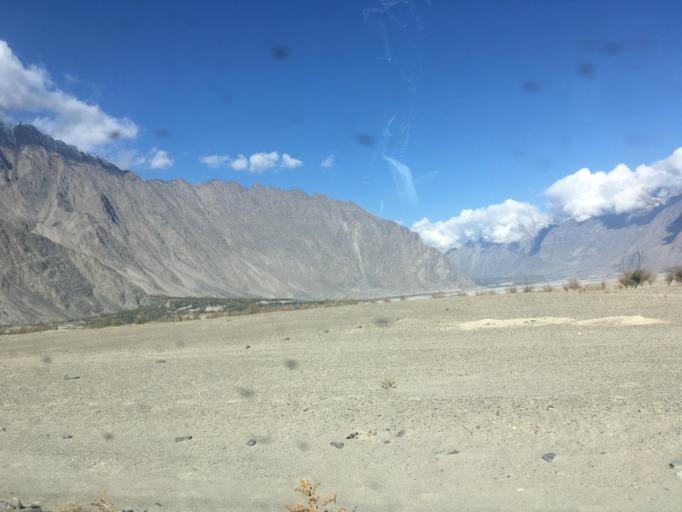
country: PK
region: Gilgit-Baltistan
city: Skardu
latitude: 35.3587
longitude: 75.5297
